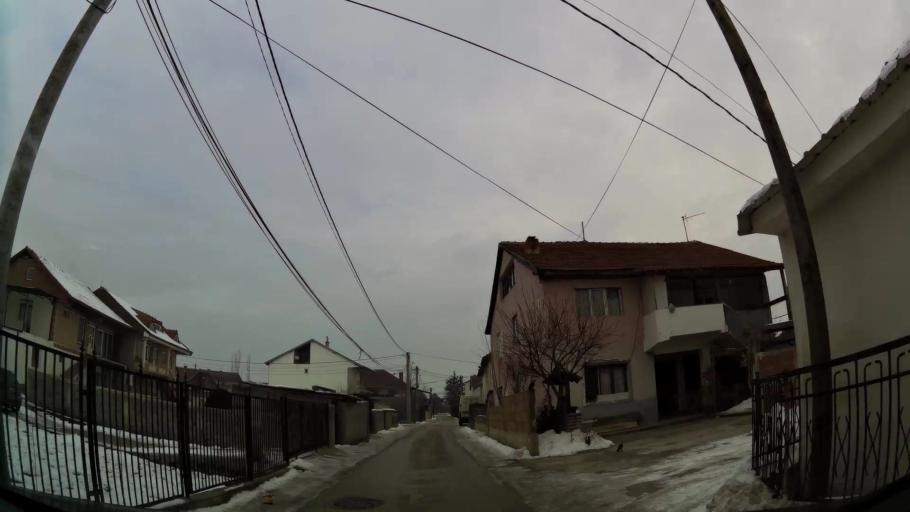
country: MK
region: Saraj
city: Saraj
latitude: 42.0473
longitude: 21.3586
